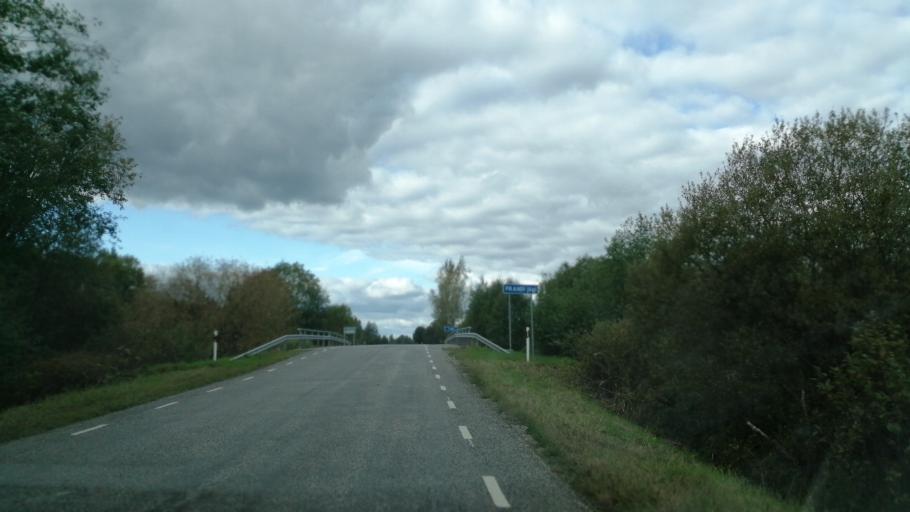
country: EE
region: Jaervamaa
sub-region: Tueri vald
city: Tueri
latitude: 58.7989
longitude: 25.4772
